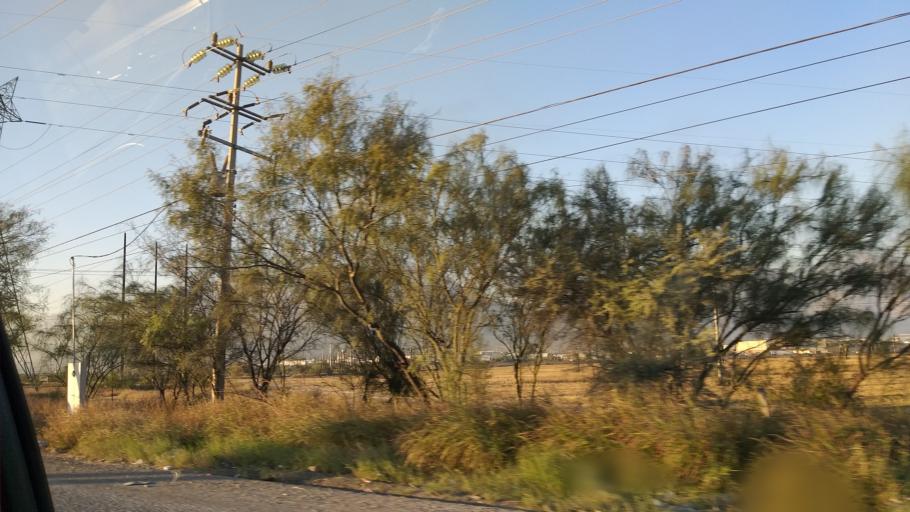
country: MX
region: Nuevo Leon
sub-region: Garcia
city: Parque Industrial Ciudad Mitras
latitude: 25.7773
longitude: -100.4418
